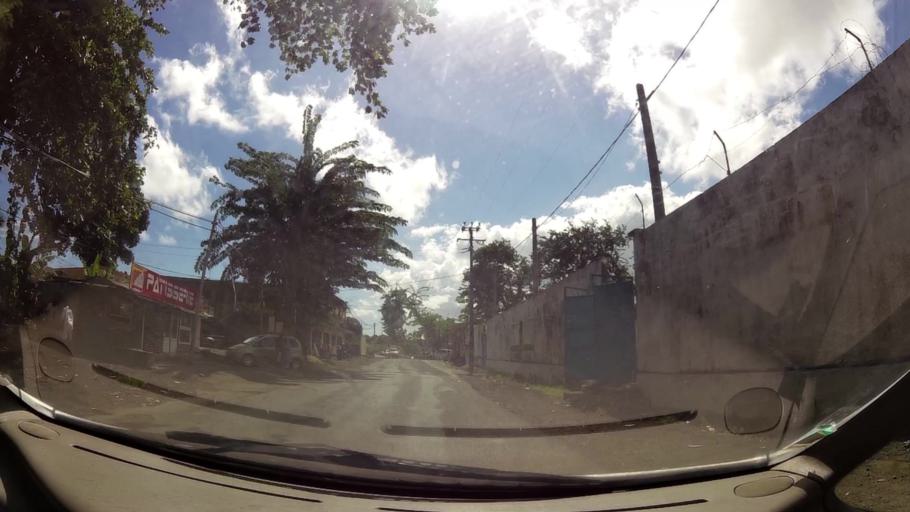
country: KM
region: Grande Comore
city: Mavingouni
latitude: -11.7372
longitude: 43.2503
